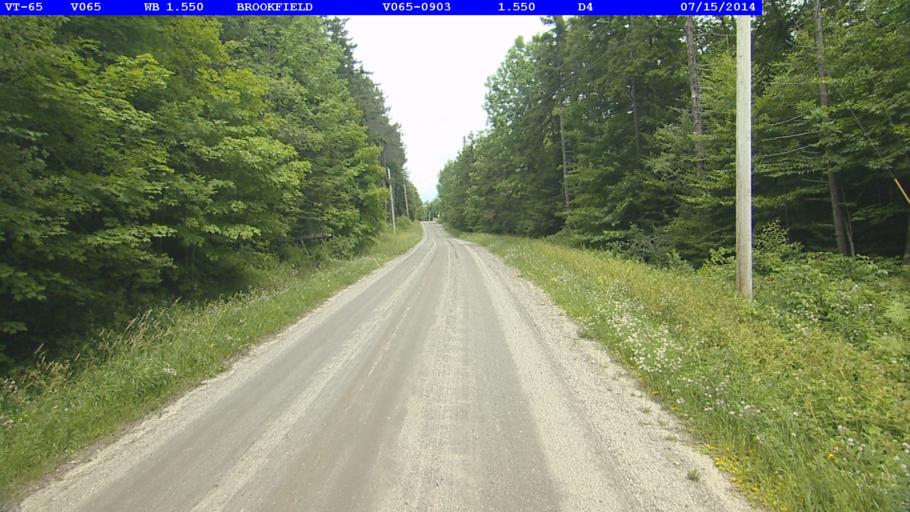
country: US
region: Vermont
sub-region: Washington County
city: Northfield
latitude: 44.0485
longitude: -72.6257
